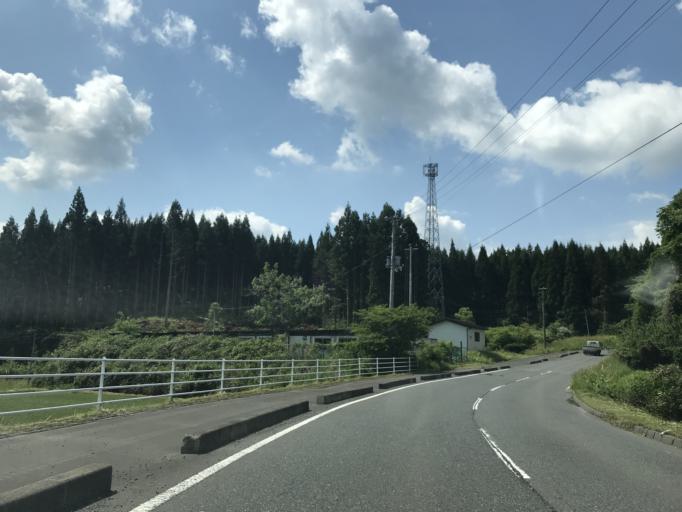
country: JP
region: Miyagi
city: Furukawa
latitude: 38.7030
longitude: 140.9289
